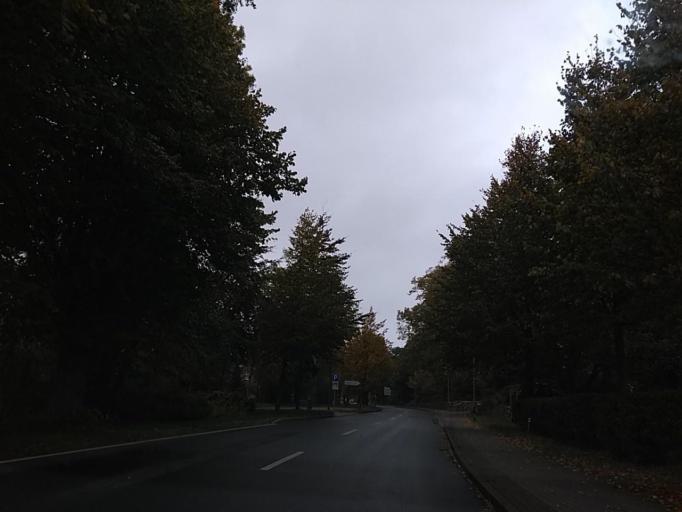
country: DE
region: Mecklenburg-Vorpommern
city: Ostseebad Kuhlungsborn
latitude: 54.1367
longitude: 11.7503
